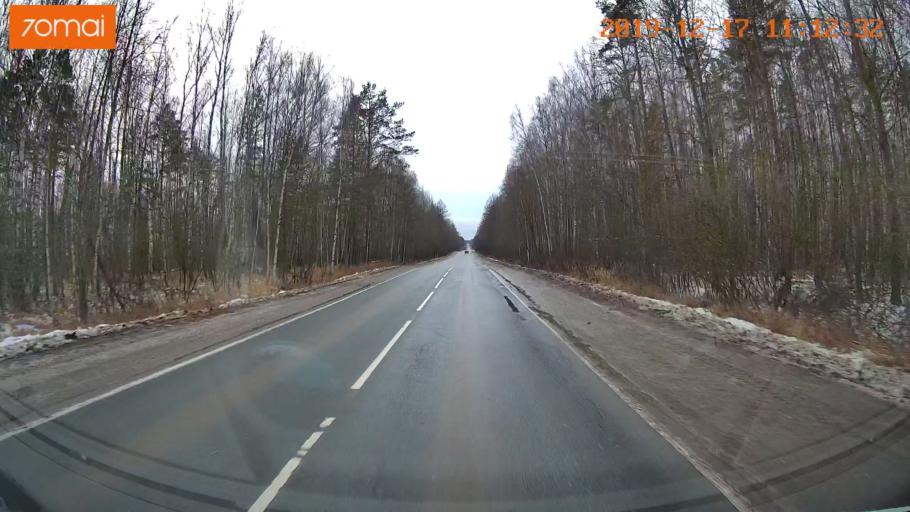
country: RU
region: Vladimir
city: Gus'-Khrustal'nyy
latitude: 55.5745
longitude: 40.6274
